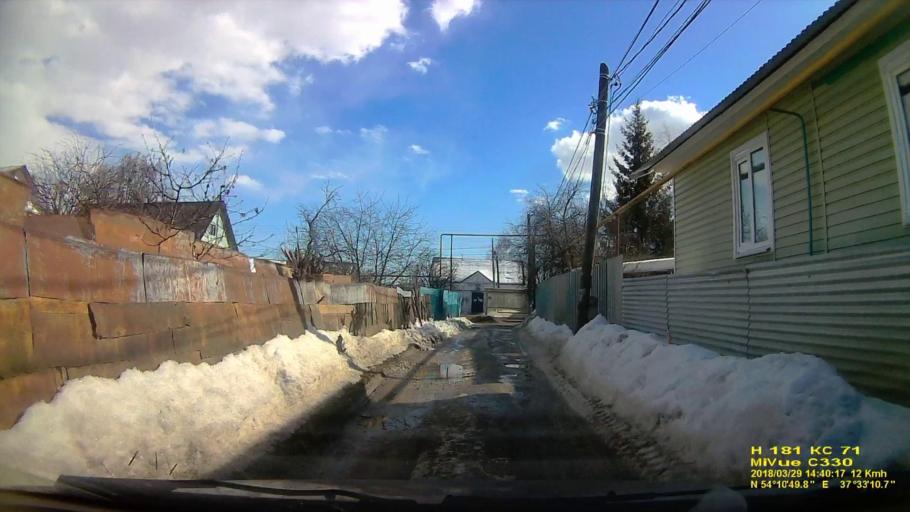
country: RU
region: Tula
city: Mendeleyevskiy
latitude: 54.1805
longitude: 37.5530
